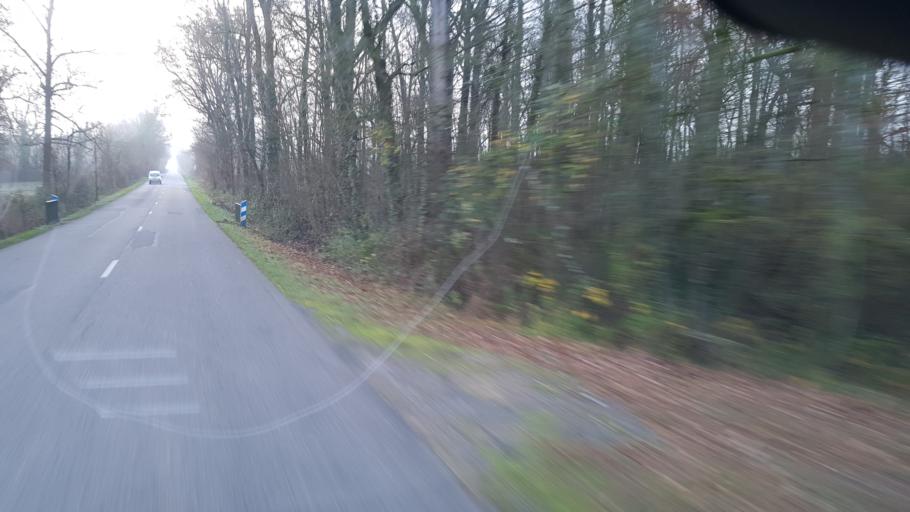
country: FR
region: Midi-Pyrenees
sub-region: Departement du Tarn-et-Garonne
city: Monteils
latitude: 44.1186
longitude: 1.5890
